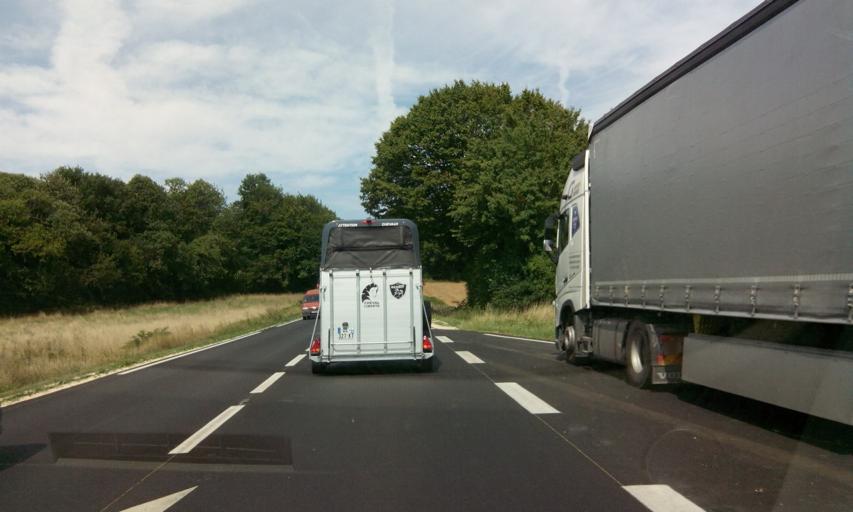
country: FR
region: Poitou-Charentes
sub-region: Departement des Deux-Sevres
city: Sauze-Vaussais
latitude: 46.1501
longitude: 0.0644
